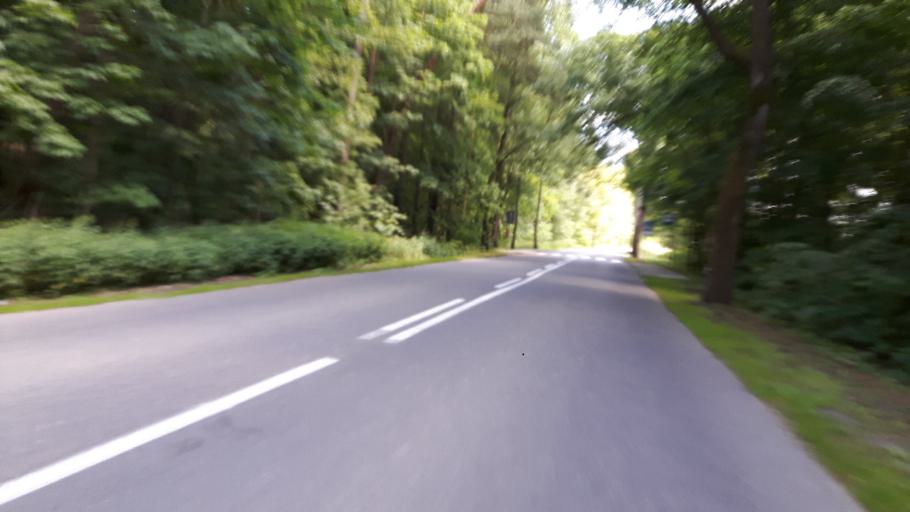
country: PL
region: Pomeranian Voivodeship
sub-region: Powiat gdanski
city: Cedry Wielkie
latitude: 54.3422
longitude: 18.8639
